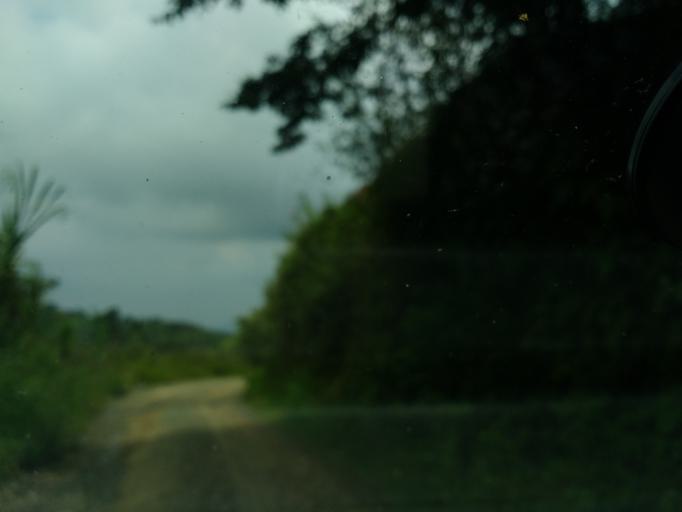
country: CO
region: Cauca
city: Santander de Quilichao
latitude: 2.9255
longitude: -76.4666
